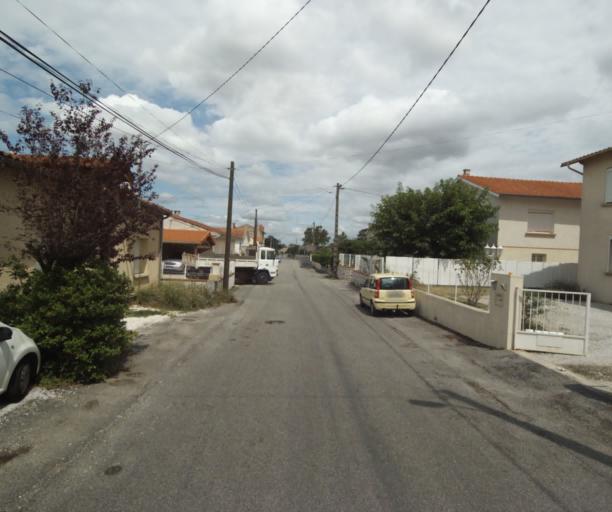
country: FR
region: Midi-Pyrenees
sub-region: Departement de la Haute-Garonne
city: Revel
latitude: 43.4535
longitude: 1.9987
